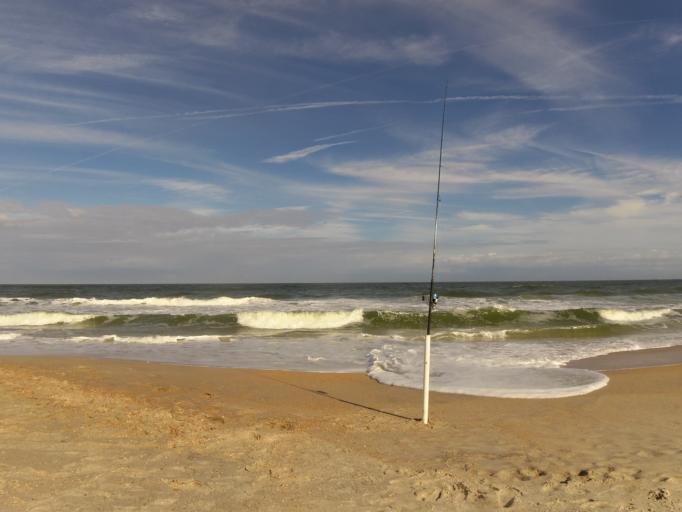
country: US
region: Florida
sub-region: Saint Johns County
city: Villano Beach
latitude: 29.9232
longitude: -81.2930
